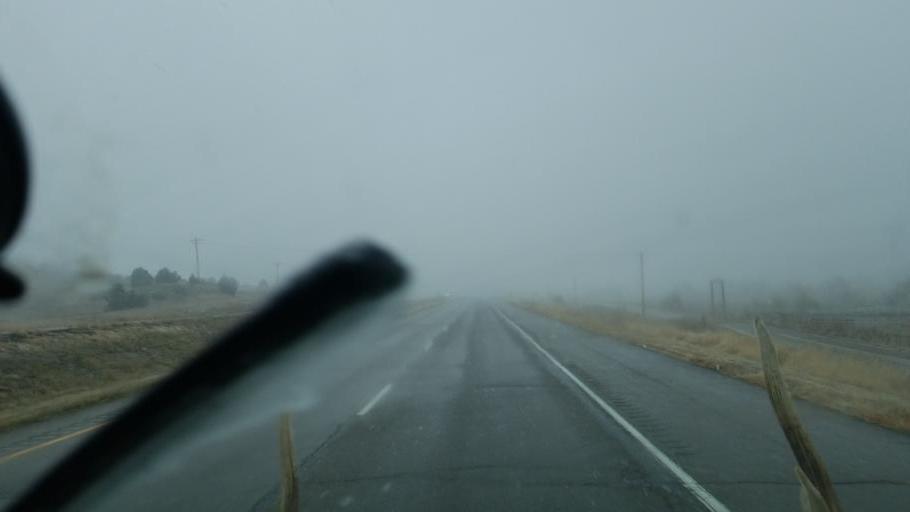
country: US
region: Colorado
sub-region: Pueblo County
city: Colorado City
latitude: 38.0139
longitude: -104.7443
